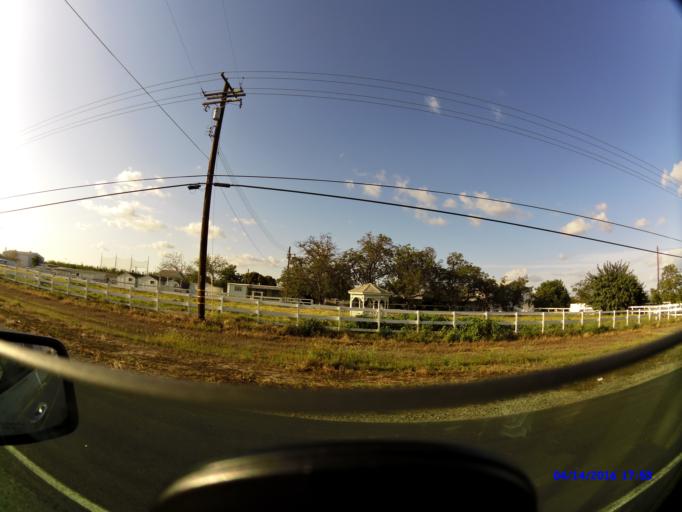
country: US
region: California
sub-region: Stanislaus County
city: Del Rio
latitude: 37.7112
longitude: -120.9908
